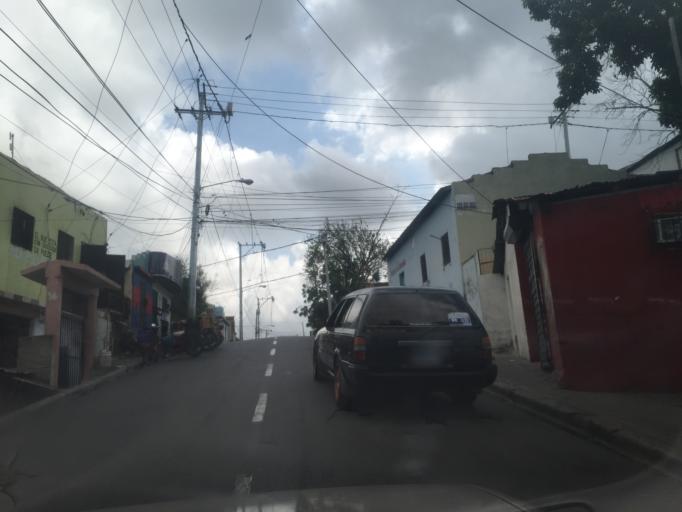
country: DO
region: Santiago
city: Santiago de los Caballeros
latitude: 19.4247
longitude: -70.7168
